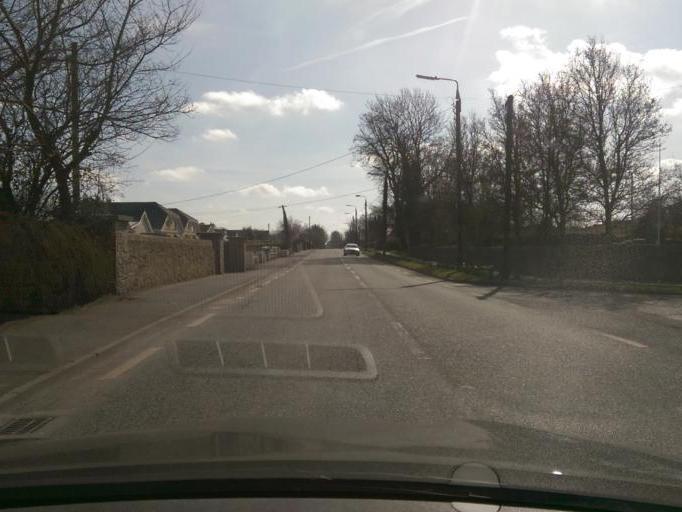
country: IE
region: Leinster
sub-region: Kildare
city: Maynooth
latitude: 53.3907
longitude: -6.5985
